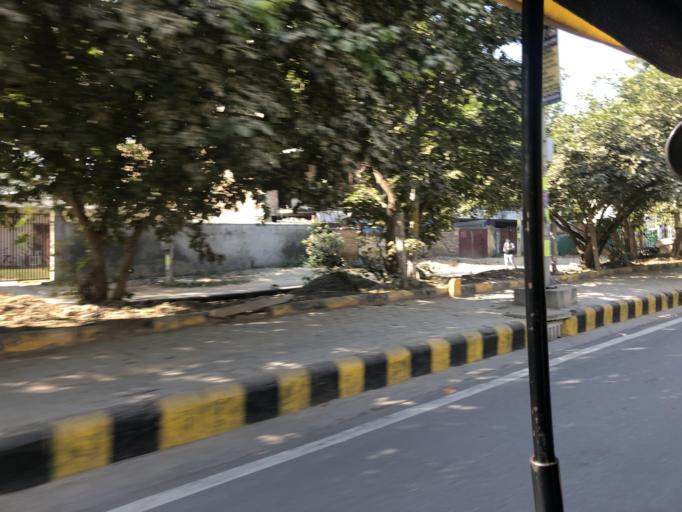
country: IN
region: Haryana
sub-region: Gurgaon
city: Gurgaon
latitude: 28.4512
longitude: 77.0680
